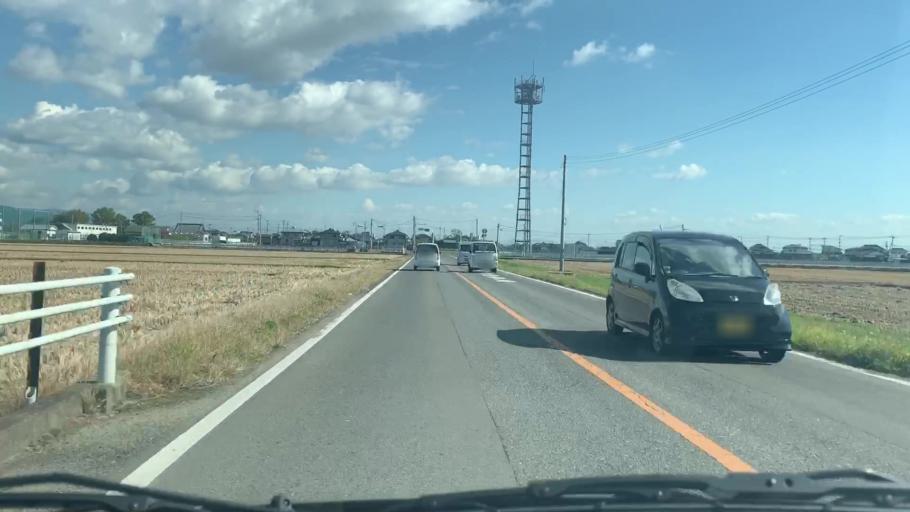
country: JP
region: Saga Prefecture
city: Saga-shi
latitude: 33.2783
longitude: 130.2214
